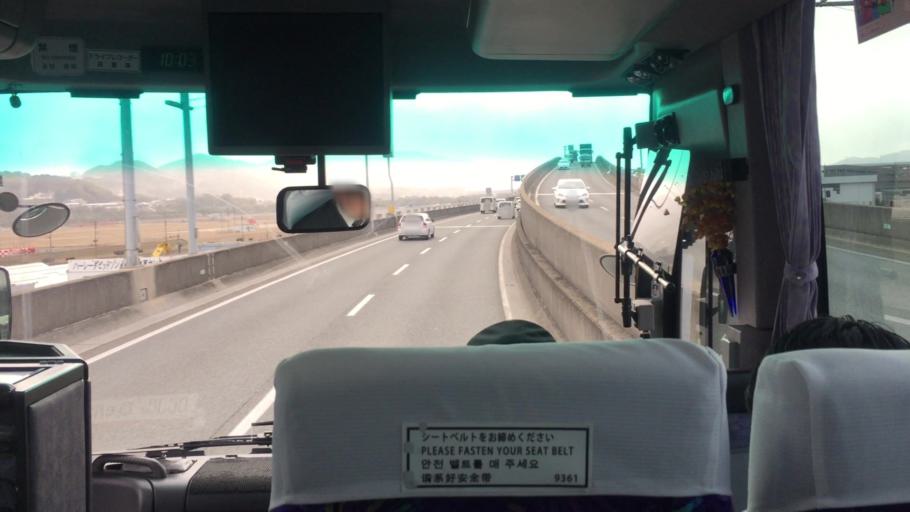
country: JP
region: Fukuoka
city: Fukuoka-shi
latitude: 33.5752
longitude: 130.4517
